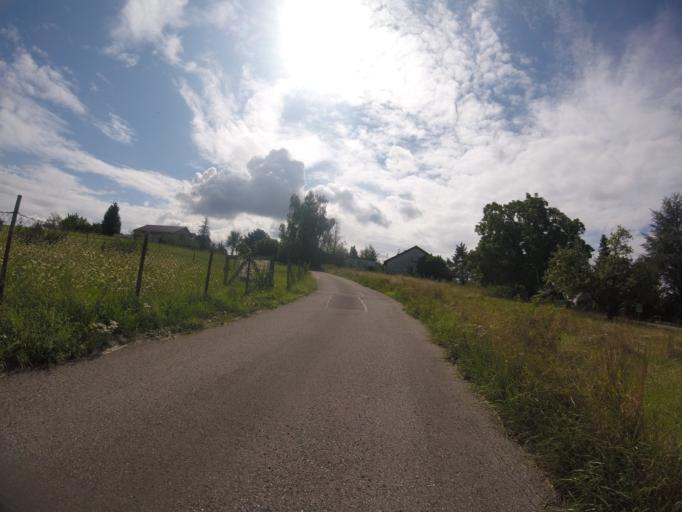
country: DE
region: Baden-Wuerttemberg
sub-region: Regierungsbezirk Stuttgart
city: Winnenden
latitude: 48.8563
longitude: 9.4073
